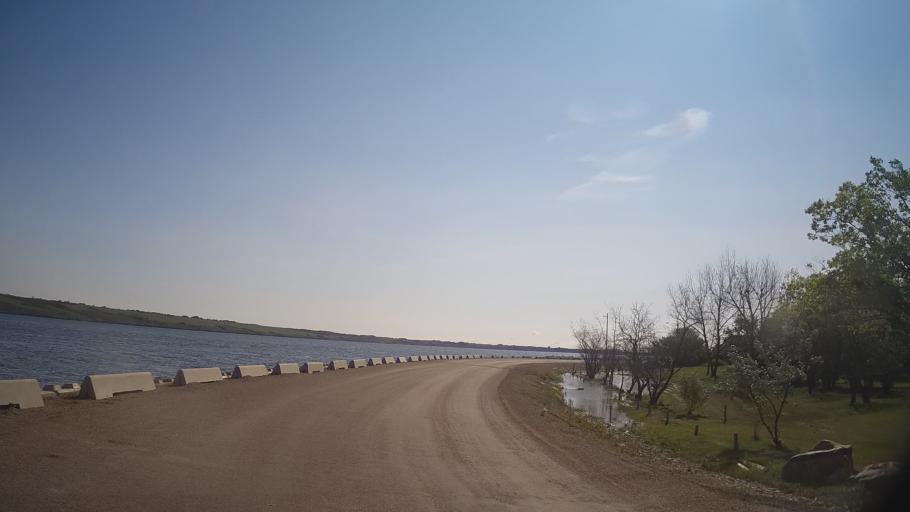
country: CA
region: Saskatchewan
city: Watrous
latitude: 51.7190
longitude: -105.4322
